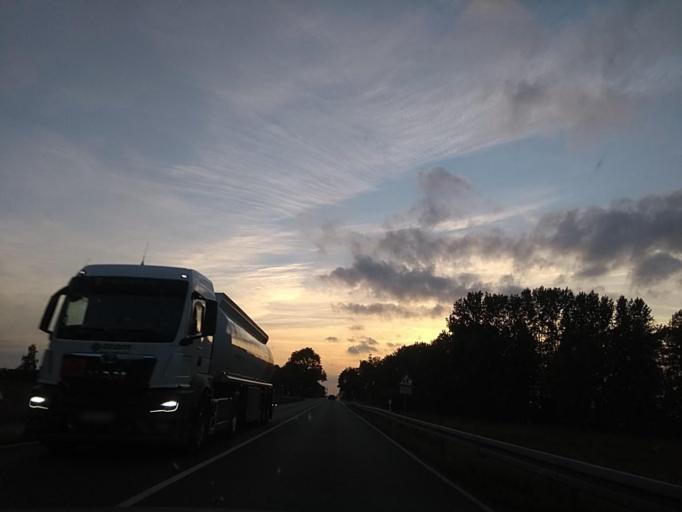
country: DE
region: Mecklenburg-Vorpommern
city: Saal
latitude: 54.2604
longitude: 12.5125
